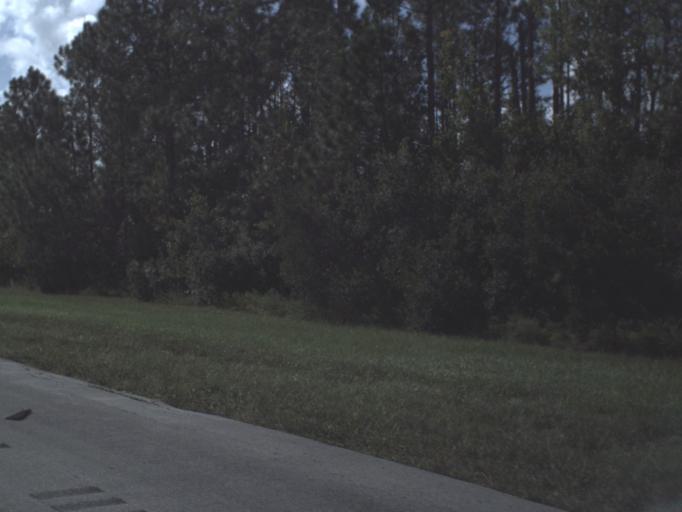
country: US
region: Florida
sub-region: Osceola County
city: Saint Cloud
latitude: 27.9153
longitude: -81.0547
